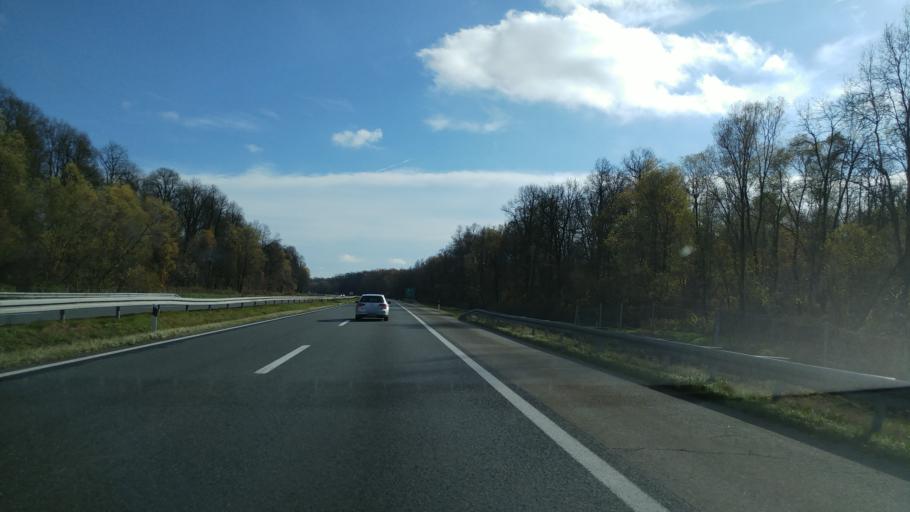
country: HR
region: Sisacko-Moslavacka
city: Lipovljani
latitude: 45.3450
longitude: 16.9176
